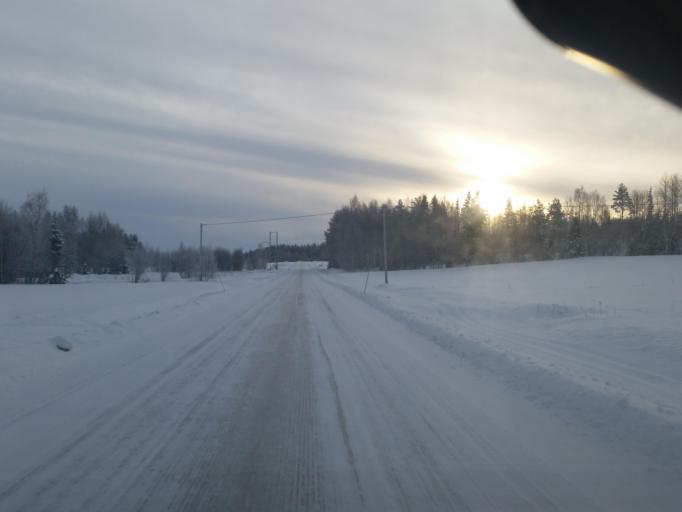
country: SE
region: Norrbotten
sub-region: Pitea Kommun
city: Norrfjarden
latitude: 65.5493
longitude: 21.4863
